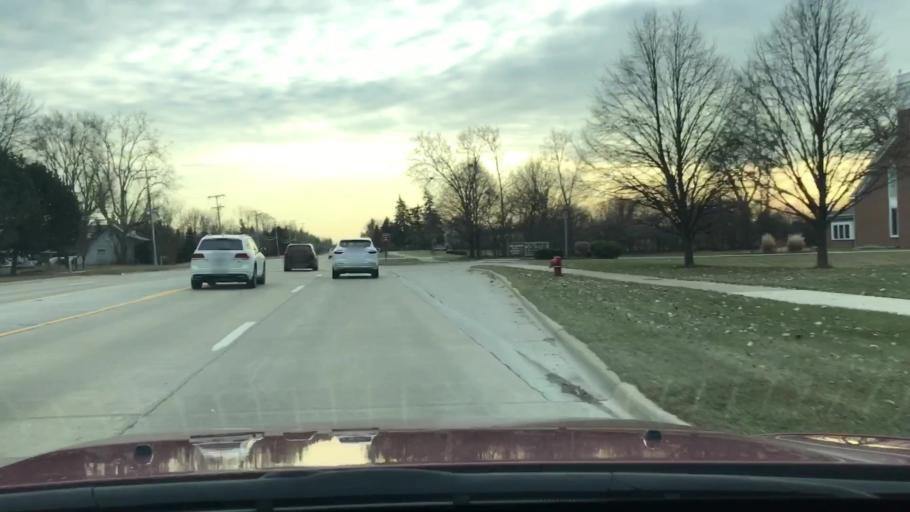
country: US
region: Michigan
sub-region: Oakland County
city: Troy
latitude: 42.5754
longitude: -83.1092
